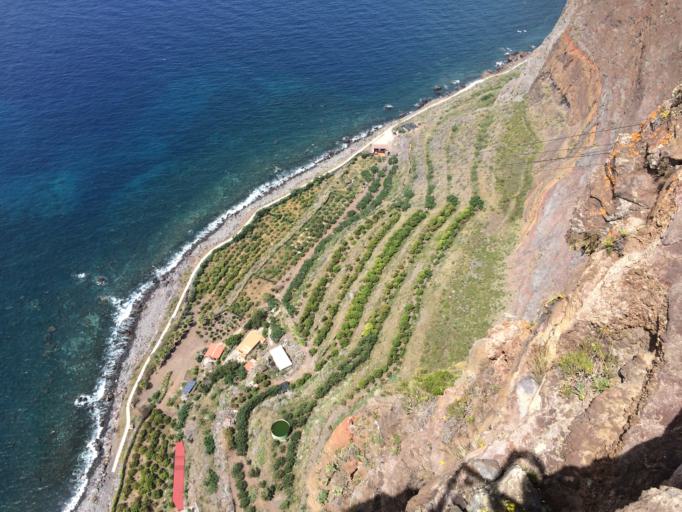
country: PT
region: Madeira
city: Camara de Lobos
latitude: 32.6525
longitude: -16.9926
